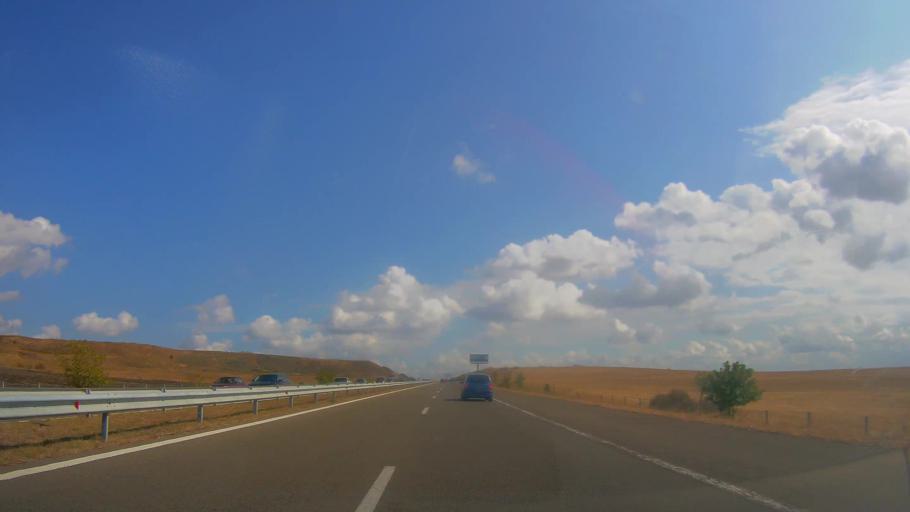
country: BG
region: Burgas
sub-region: Obshtina Kameno
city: Kameno
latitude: 42.5928
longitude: 27.1746
